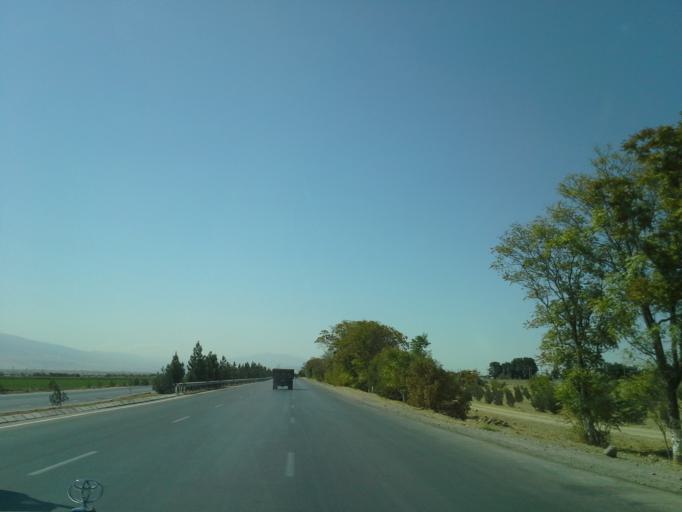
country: TM
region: Ahal
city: Annau
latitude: 37.9054
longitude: 58.5366
